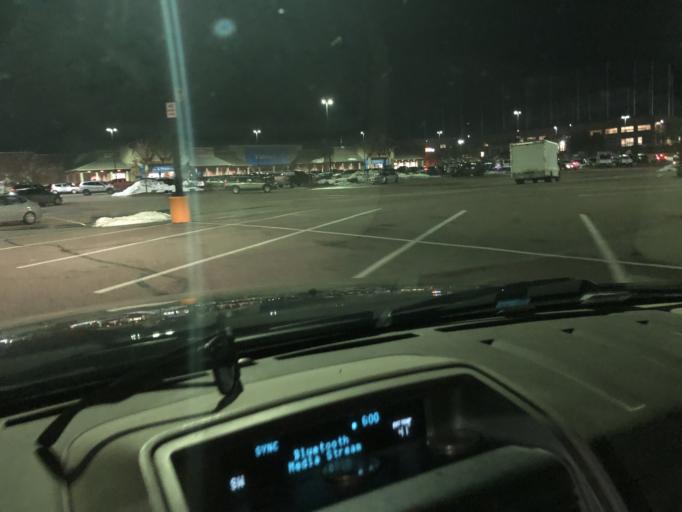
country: US
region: Colorado
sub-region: Arapahoe County
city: Centennial
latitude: 39.5923
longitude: -104.8608
